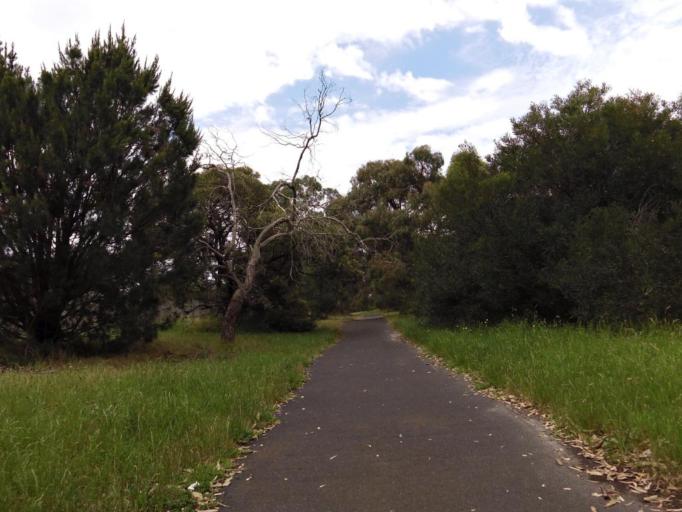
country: AU
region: Victoria
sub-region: Greater Dandenong
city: Springvale South
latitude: -37.9654
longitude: 145.1358
